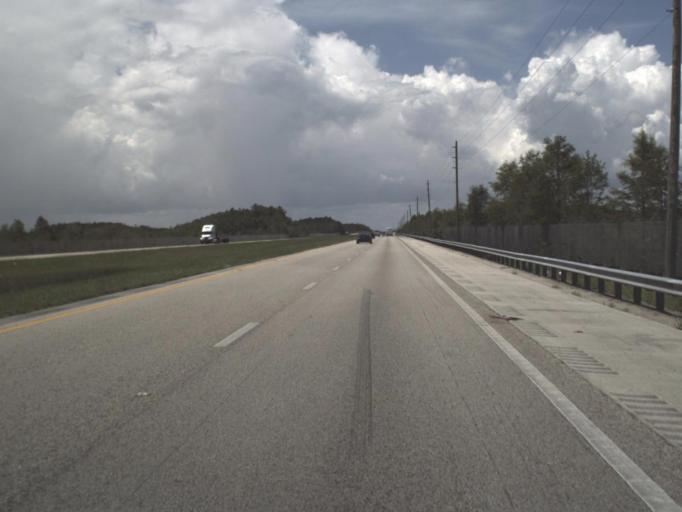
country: US
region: Florida
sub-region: Collier County
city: Immokalee
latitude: 26.1679
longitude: -81.1415
